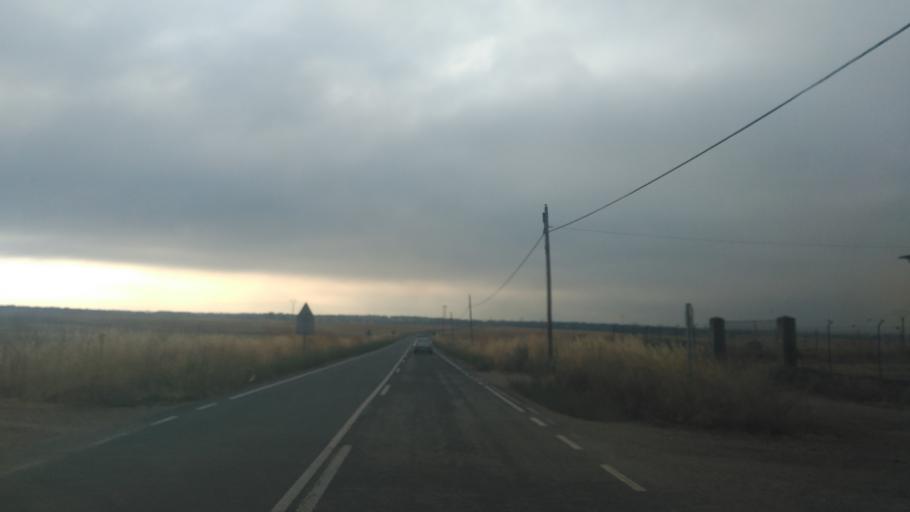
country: ES
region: Castille and Leon
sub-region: Provincia de Salamanca
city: Robliza de Cojos
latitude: 40.8657
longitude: -5.9726
